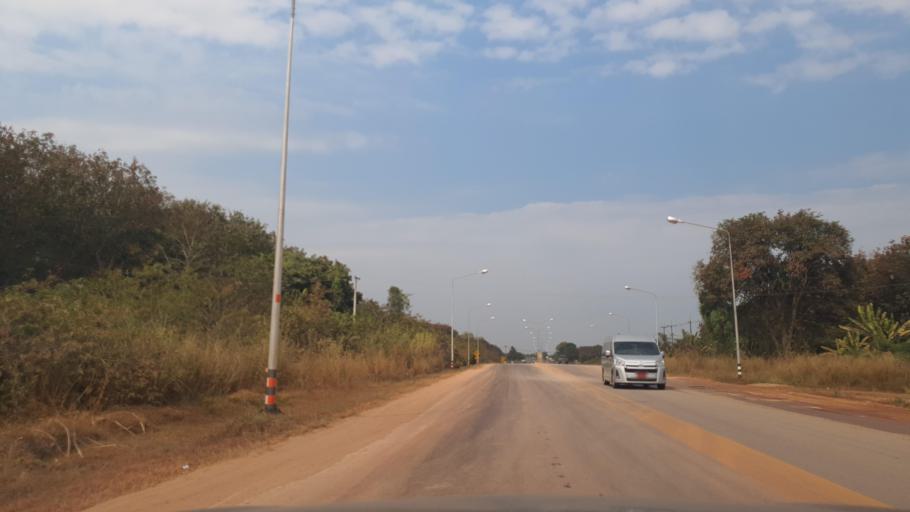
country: TH
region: Changwat Bueng Kan
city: Si Wilai
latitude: 18.2946
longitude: 103.8200
